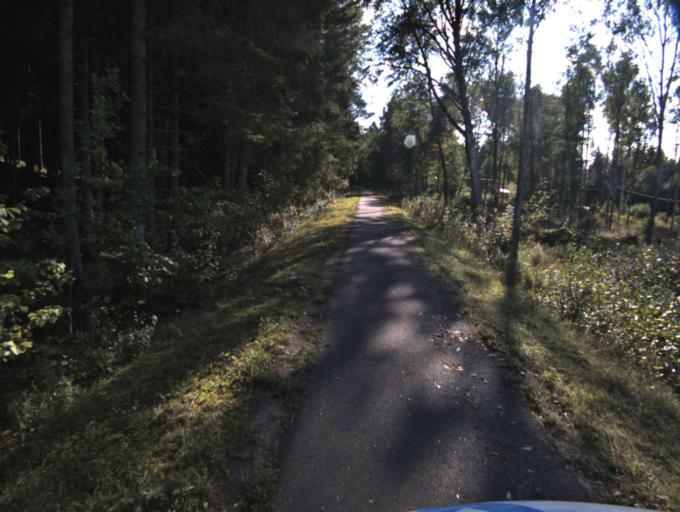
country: SE
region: Vaestra Goetaland
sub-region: Boras Kommun
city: Dalsjofors
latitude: 57.8134
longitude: 13.1389
